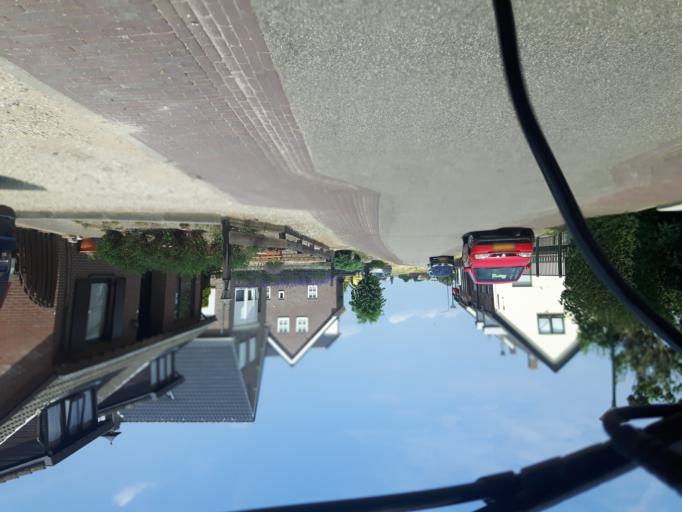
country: NL
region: Gelderland
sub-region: Gemeente Zaltbommel
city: Zaltbommel
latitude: 51.8134
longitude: 5.2153
